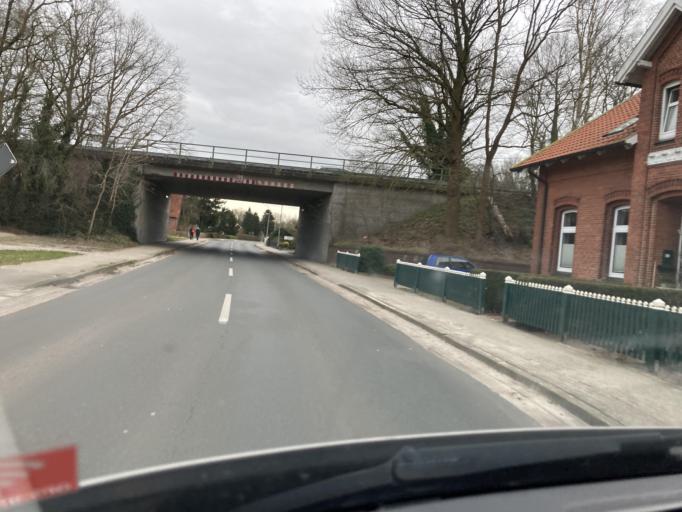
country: DE
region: Lower Saxony
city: Leer
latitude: 53.1615
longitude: 7.4604
